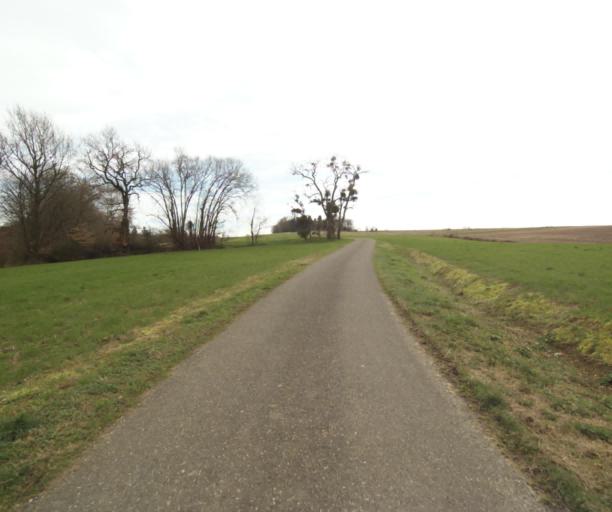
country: FR
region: Aquitaine
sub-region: Departement des Landes
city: Gabarret
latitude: 43.9229
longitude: 0.0082
